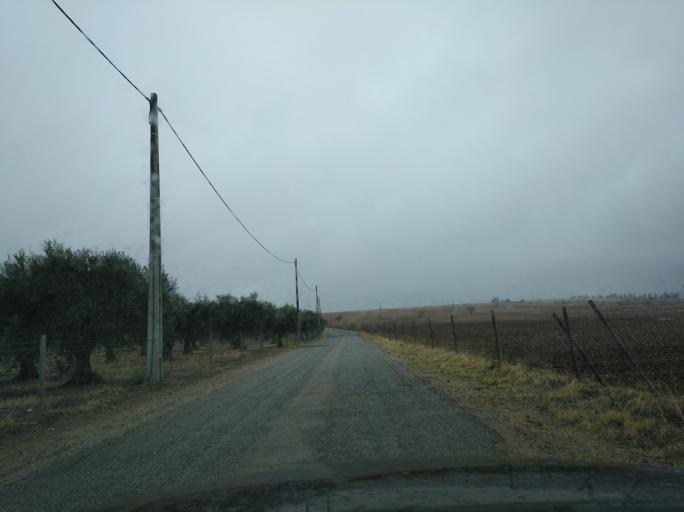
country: PT
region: Portalegre
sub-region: Campo Maior
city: Campo Maior
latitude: 38.9773
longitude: -7.0885
